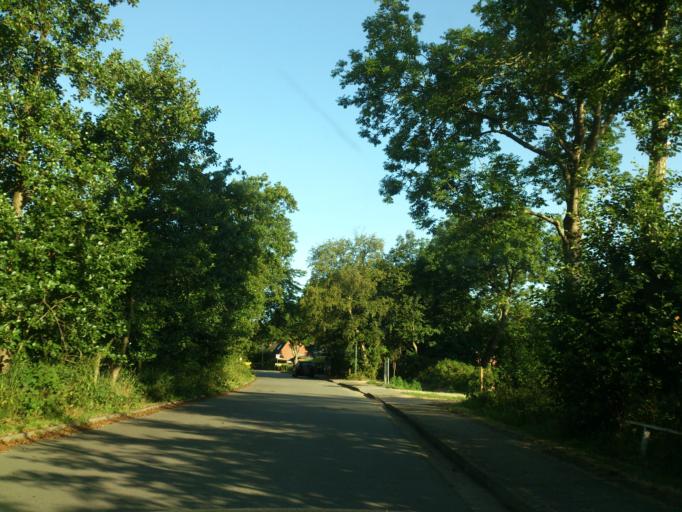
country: DE
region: Schleswig-Holstein
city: Sankt Peter-Ording
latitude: 54.3186
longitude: 8.6194
